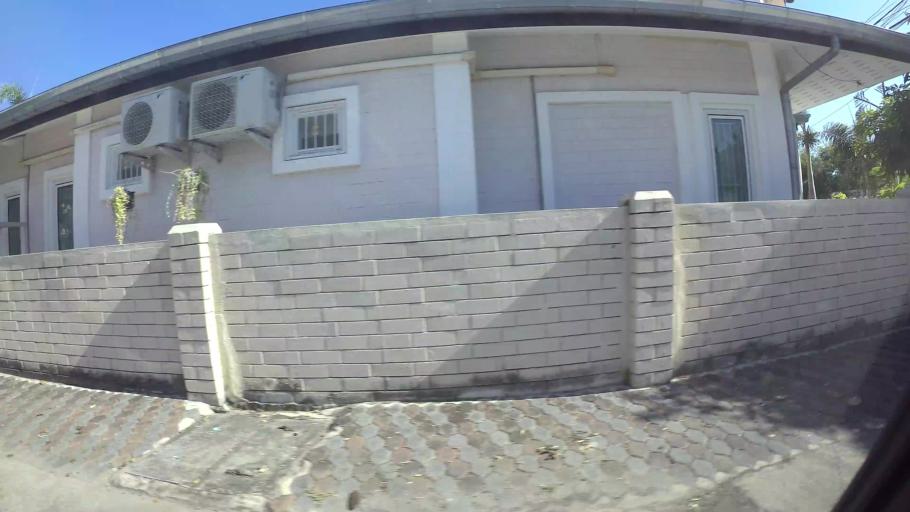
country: TH
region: Chon Buri
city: Phatthaya
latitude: 12.9079
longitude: 100.8739
